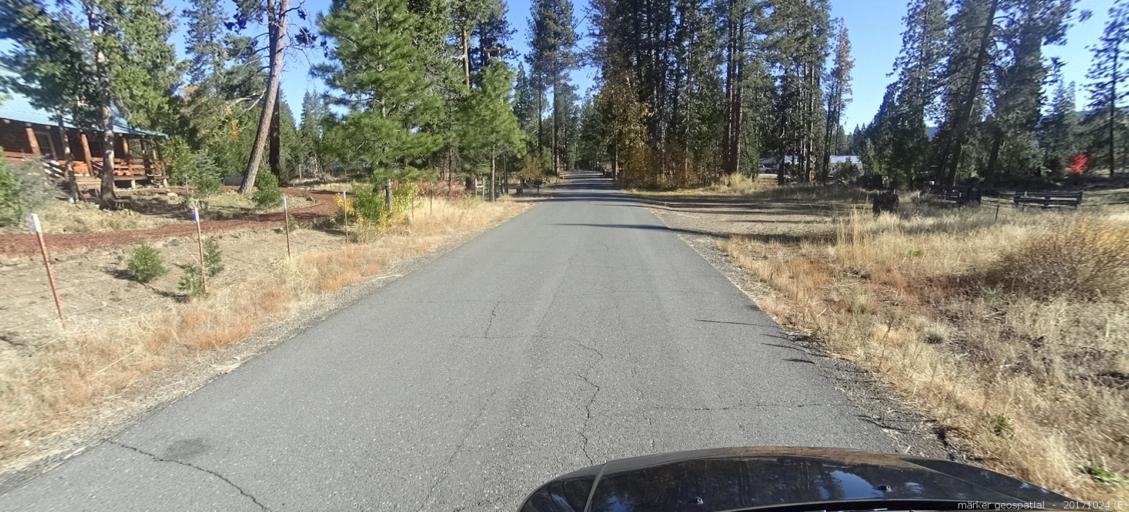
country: US
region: California
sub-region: Shasta County
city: Burney
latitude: 40.8104
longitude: -121.5082
